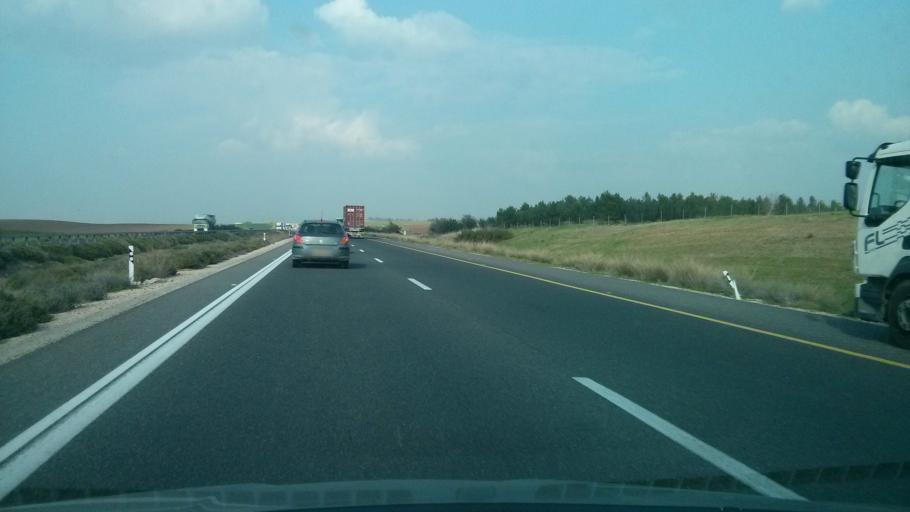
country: IL
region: Southern District
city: Qiryat Gat
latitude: 31.6930
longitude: 34.8135
